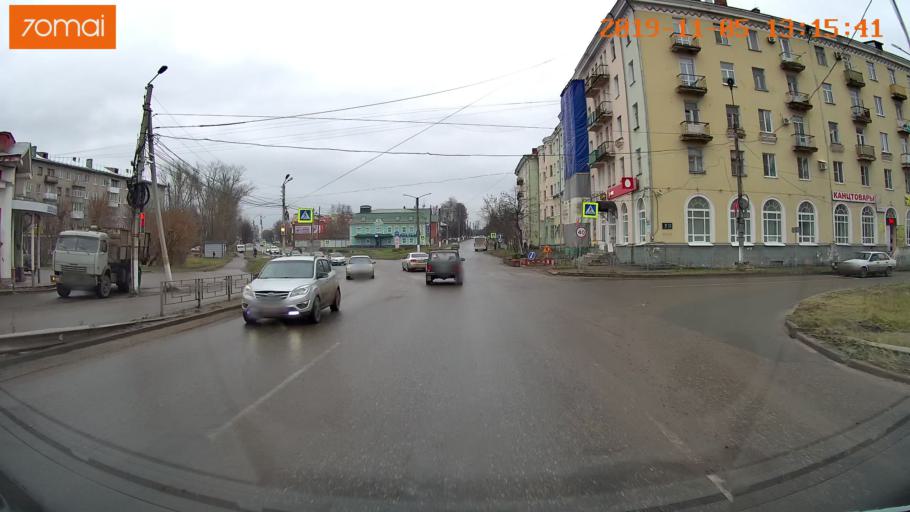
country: RU
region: Ivanovo
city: Shuya
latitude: 56.8508
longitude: 41.3678
